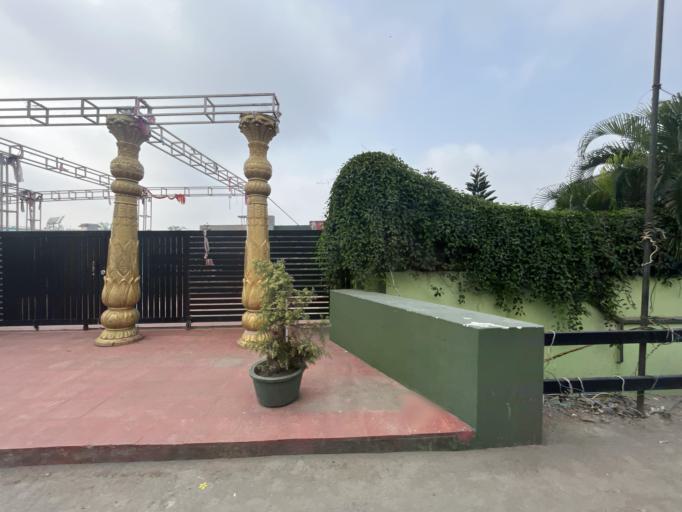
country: IN
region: Uttarakhand
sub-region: Naini Tal
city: Haldwani
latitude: 29.1942
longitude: 79.5058
